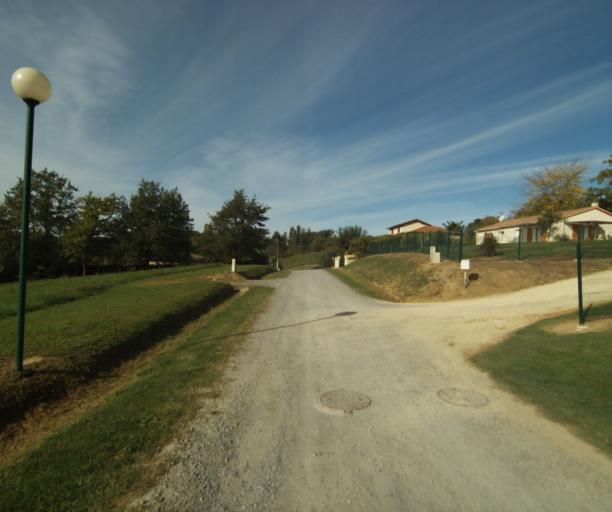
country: FR
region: Midi-Pyrenees
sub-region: Departement du Gers
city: Eauze
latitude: 43.8853
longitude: 0.1426
